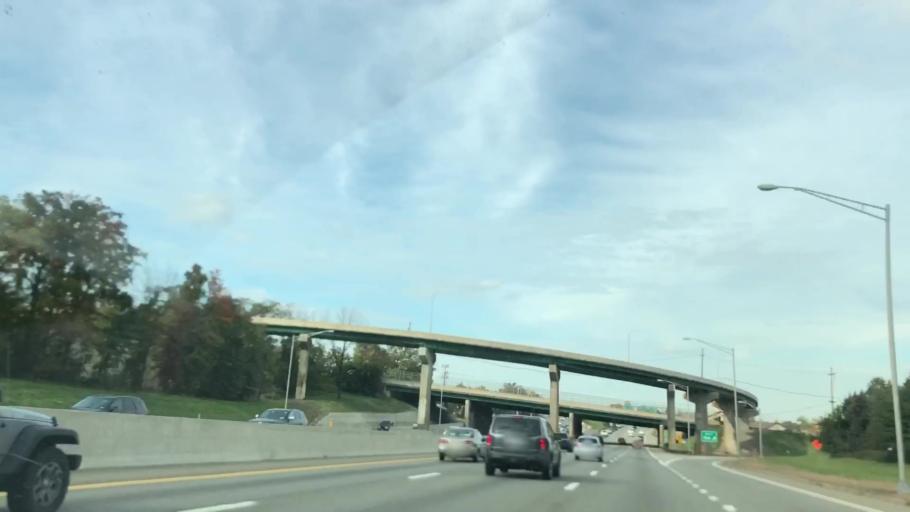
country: US
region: New Jersey
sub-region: Passaic County
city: Clifton
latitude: 40.8744
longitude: -74.1664
